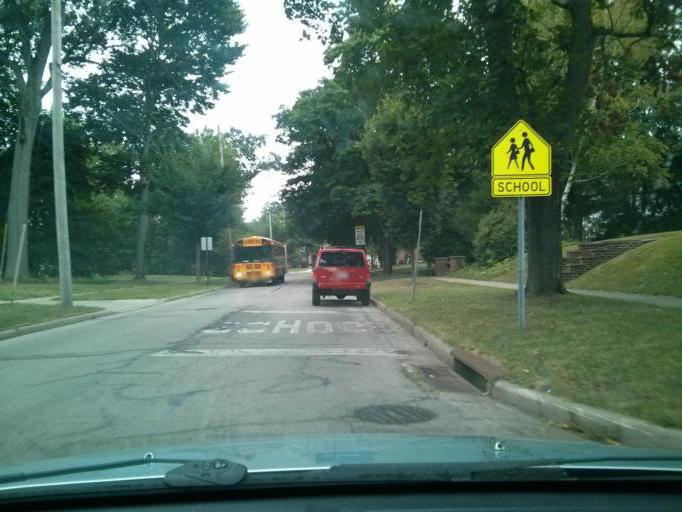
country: US
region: Ohio
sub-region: Portage County
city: Kent
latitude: 41.1555
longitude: -81.3672
